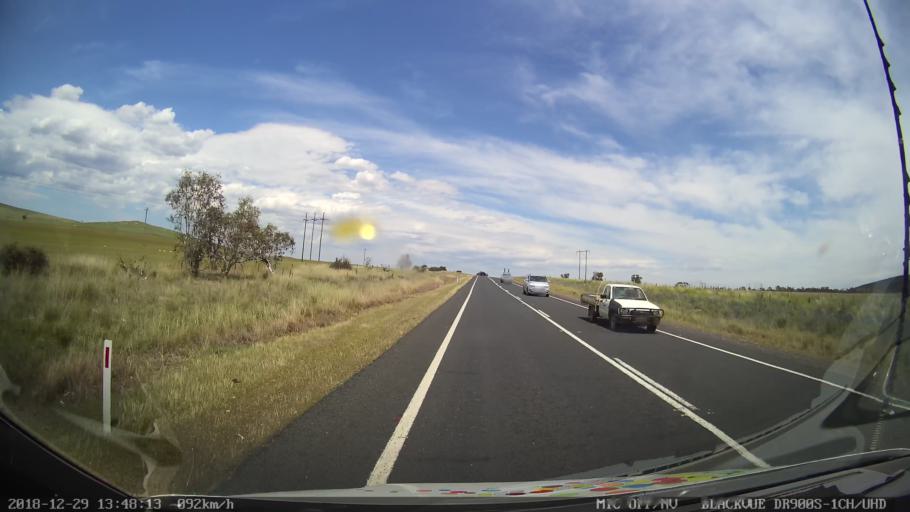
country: AU
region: New South Wales
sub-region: Cooma-Monaro
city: Cooma
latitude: -36.1374
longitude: 149.1466
